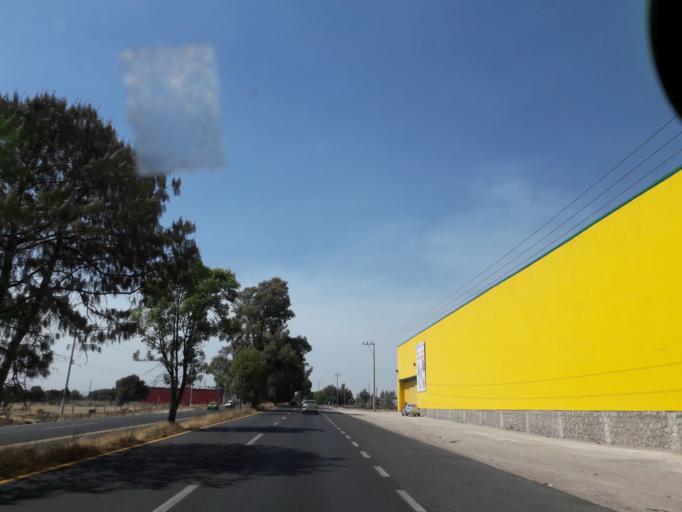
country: MX
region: Tlaxcala
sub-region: Mazatecochco de Jose Maria Morelos
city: Mazatecochco
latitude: 19.1899
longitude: -98.1941
